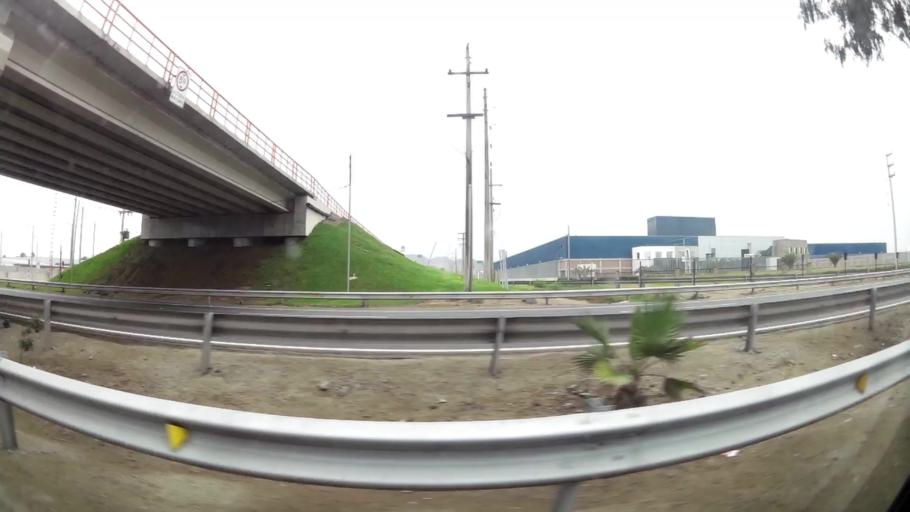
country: PE
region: Lima
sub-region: Lima
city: Punta Hermosa
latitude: -12.2835
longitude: -76.8781
